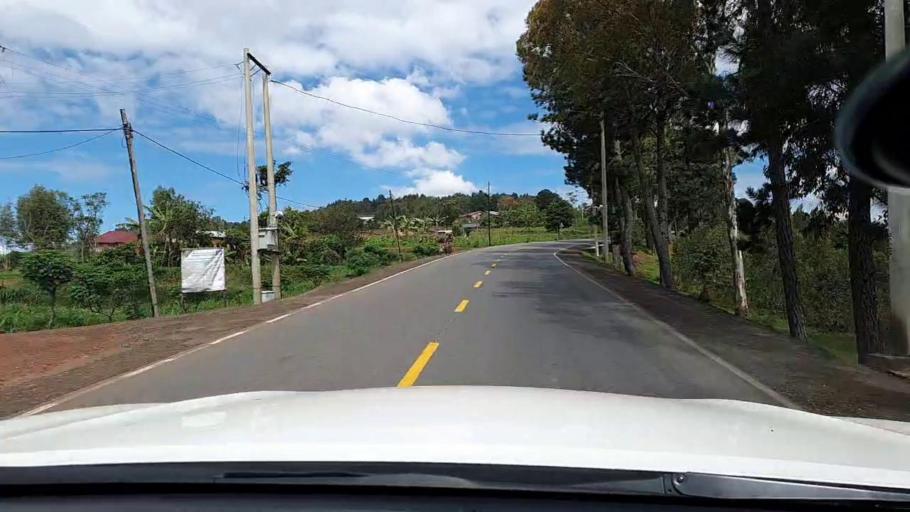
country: RW
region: Kigali
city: Kigali
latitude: -1.8307
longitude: 29.9498
